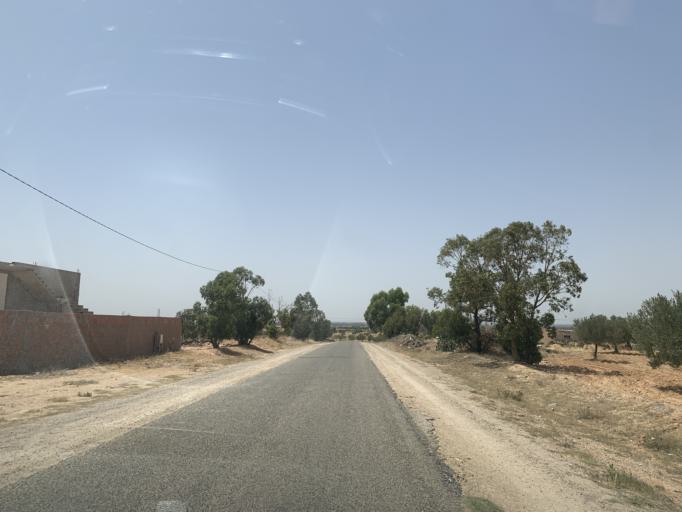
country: TN
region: Al Mahdiyah
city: Shurban
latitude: 35.1618
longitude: 10.2474
